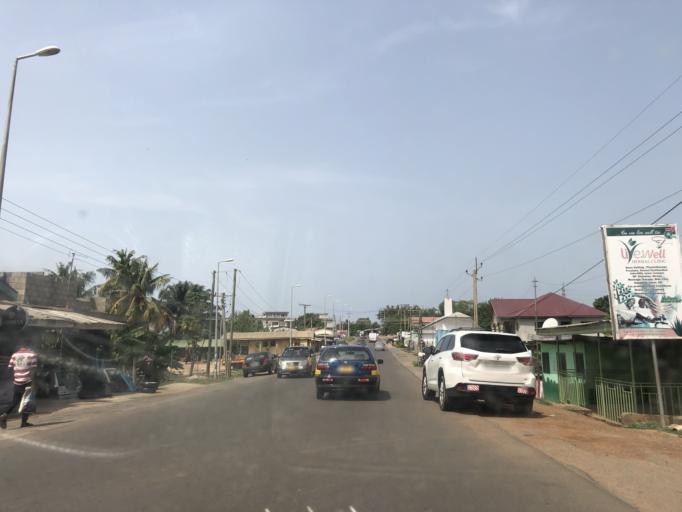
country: GH
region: Eastern
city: Koforidua
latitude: 6.0964
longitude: -0.2668
